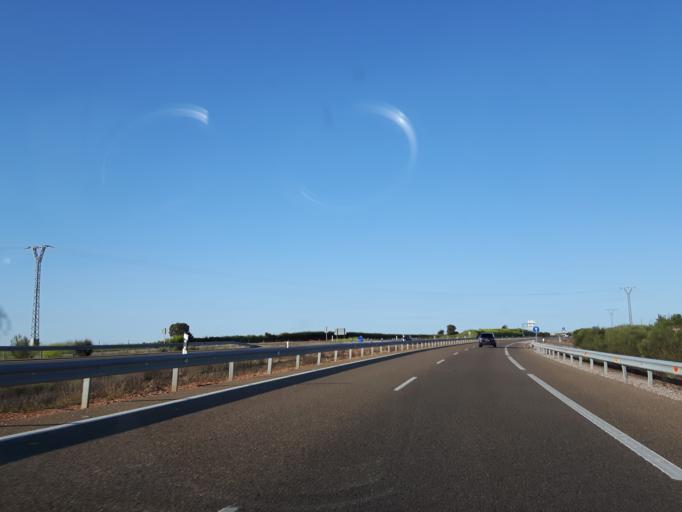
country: ES
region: Castille and Leon
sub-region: Provincia de Salamanca
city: Galindo y Perahuy
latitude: 40.9151
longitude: -5.8608
